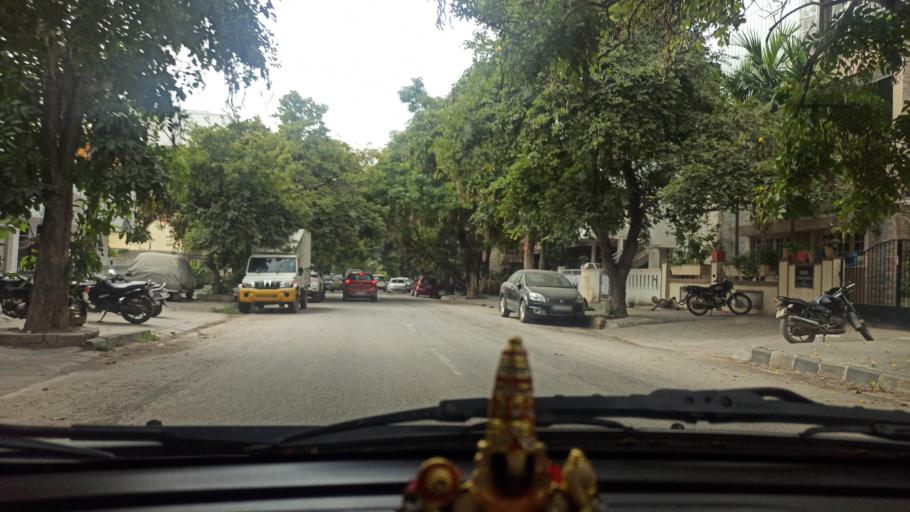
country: IN
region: Karnataka
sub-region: Bangalore Urban
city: Bangalore
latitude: 13.0184
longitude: 77.6493
